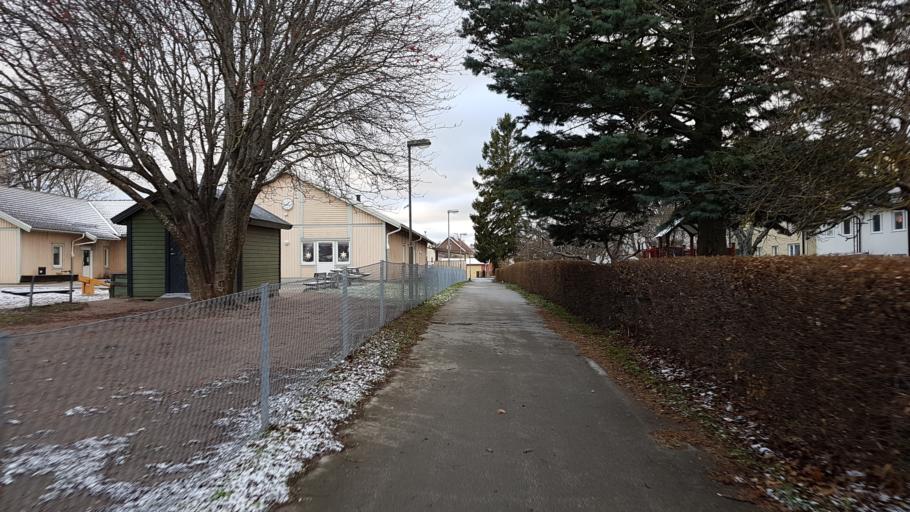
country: SE
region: Gotland
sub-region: Gotland
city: Visby
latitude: 57.6204
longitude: 18.2907
